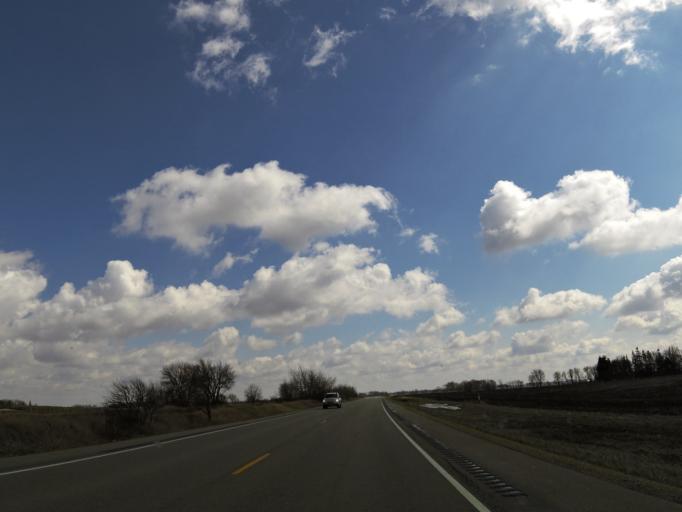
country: US
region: Minnesota
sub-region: Goodhue County
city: Kenyon
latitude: 44.2376
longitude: -92.9560
